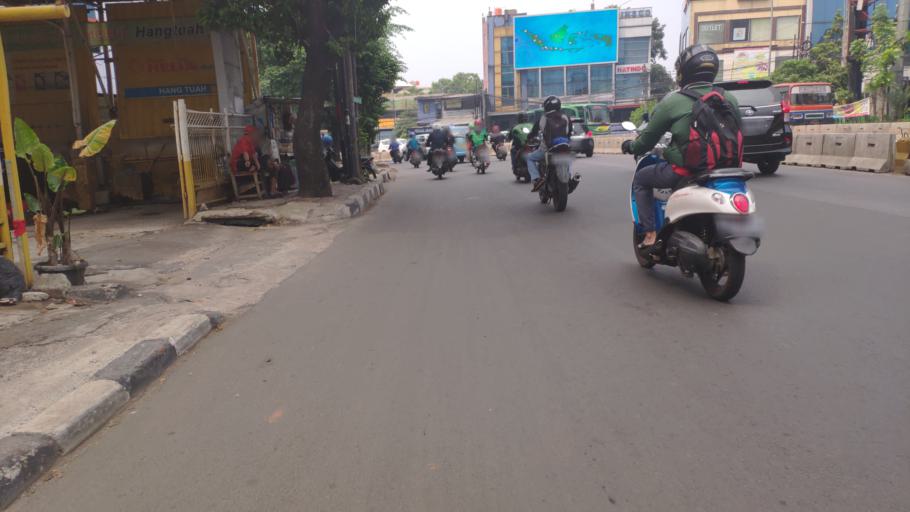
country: ID
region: Jakarta Raya
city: Jakarta
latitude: -6.2634
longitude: 106.8305
